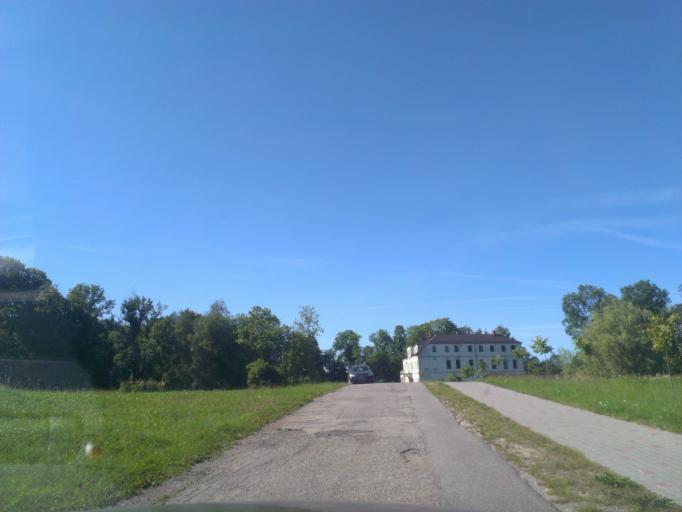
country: LV
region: Amatas Novads
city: Drabesi
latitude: 57.0673
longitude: 25.1881
